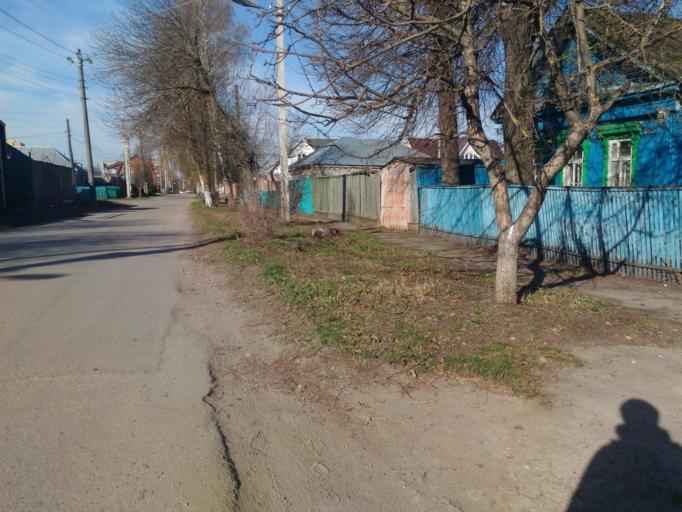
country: RU
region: Ulyanovsk
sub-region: Ulyanovskiy Rayon
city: Ulyanovsk
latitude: 54.3478
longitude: 48.3794
